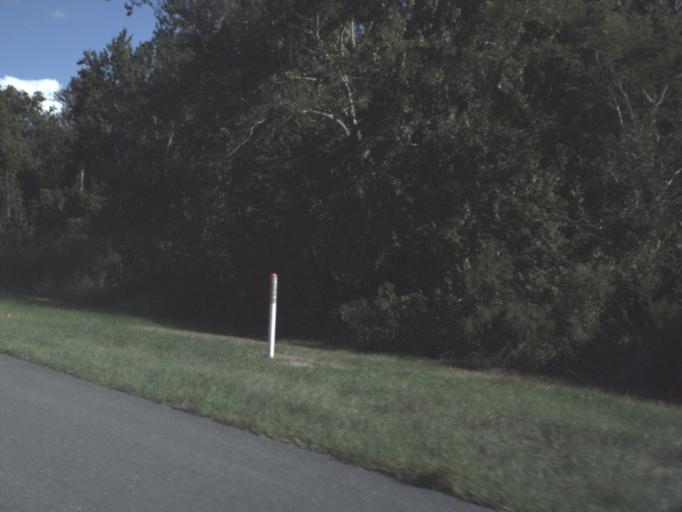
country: US
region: Florida
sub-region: Orange County
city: Winter Garden
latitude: 28.5450
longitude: -81.5954
